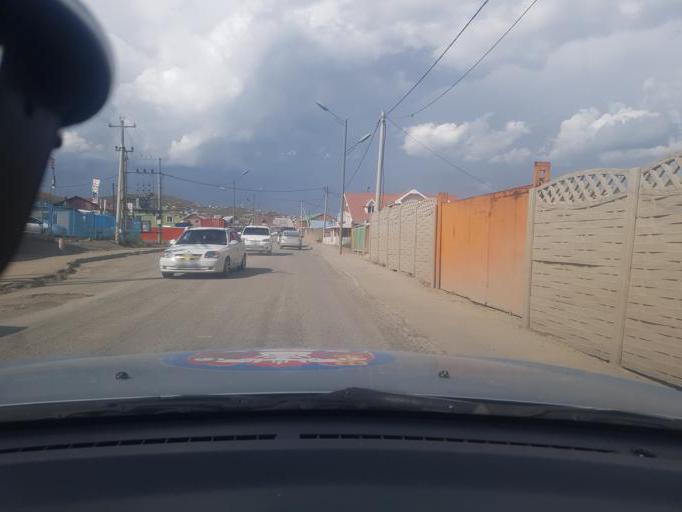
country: MN
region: Ulaanbaatar
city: Ulaanbaatar
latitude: 47.9286
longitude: 106.9660
